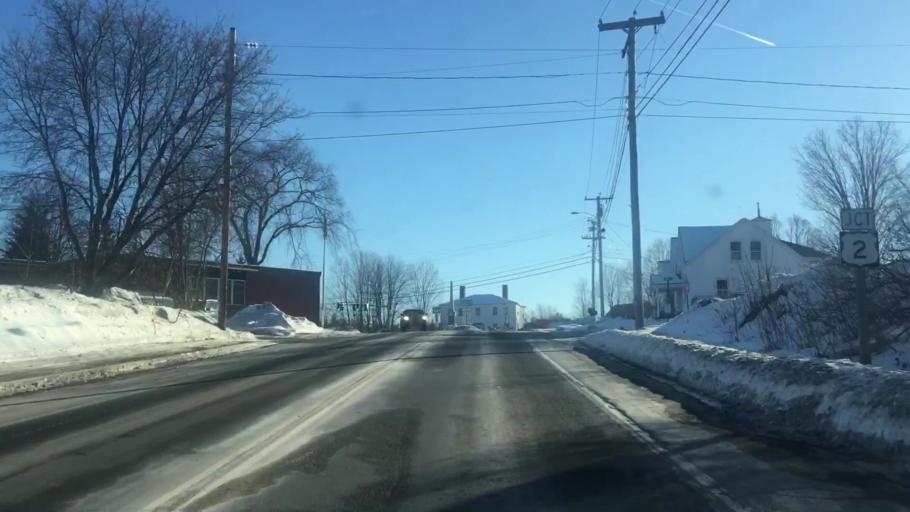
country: US
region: Maine
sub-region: Somerset County
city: Norridgewock
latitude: 44.7147
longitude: -69.7972
